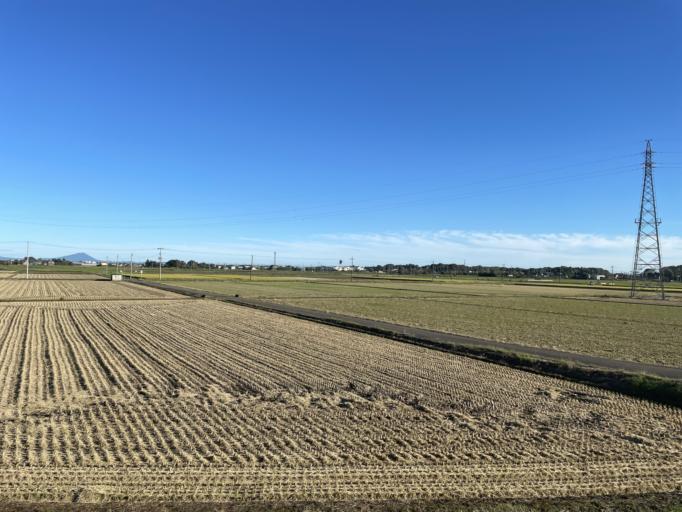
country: JP
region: Tochigi
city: Tochigi
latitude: 36.3222
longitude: 139.6907
